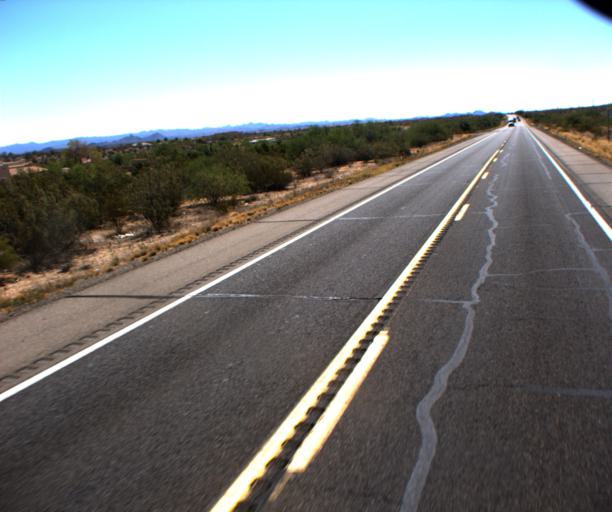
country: US
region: Arizona
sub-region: Maricopa County
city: Wickenburg
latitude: 34.0365
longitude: -112.8258
